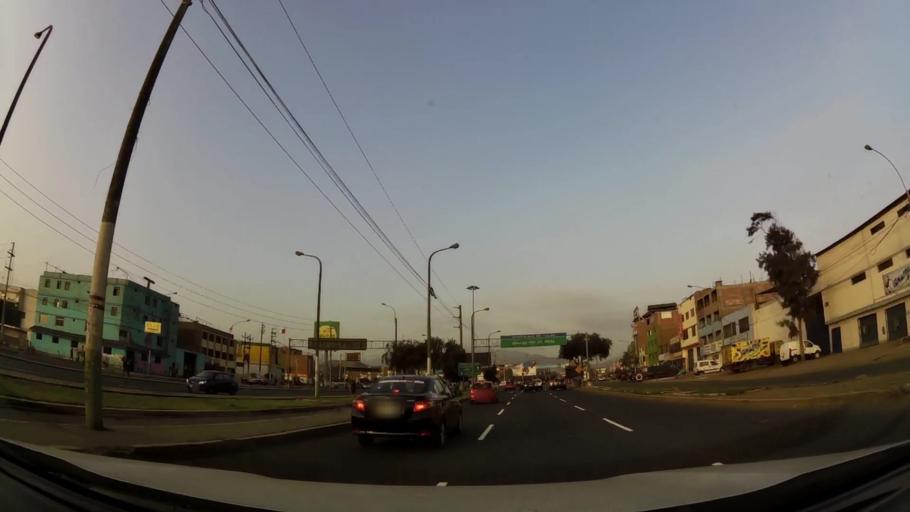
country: PE
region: Lima
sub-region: Lima
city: Independencia
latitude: -12.0119
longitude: -77.0911
